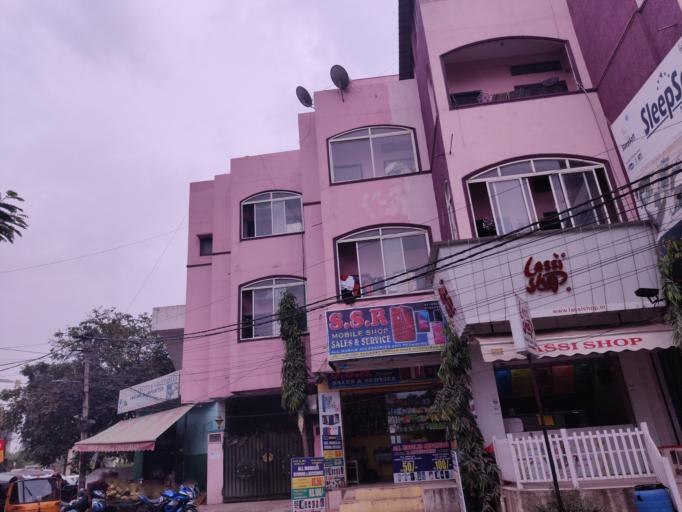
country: IN
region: Telangana
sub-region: Hyderabad
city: Hyderabad
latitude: 17.4086
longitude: 78.3943
